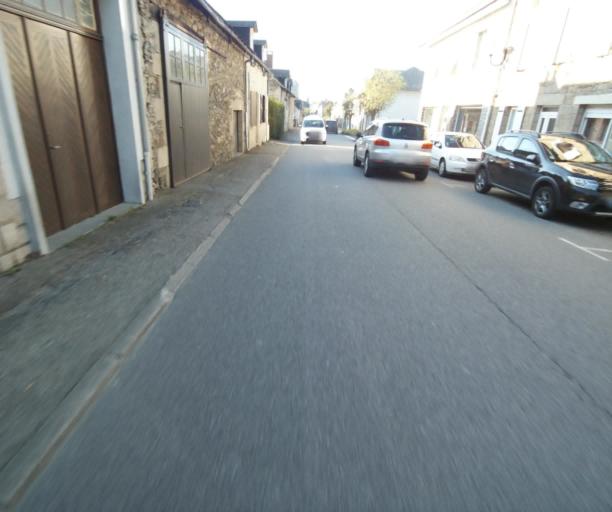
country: FR
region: Limousin
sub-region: Departement de la Correze
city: Chamboulive
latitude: 45.4292
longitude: 1.7073
